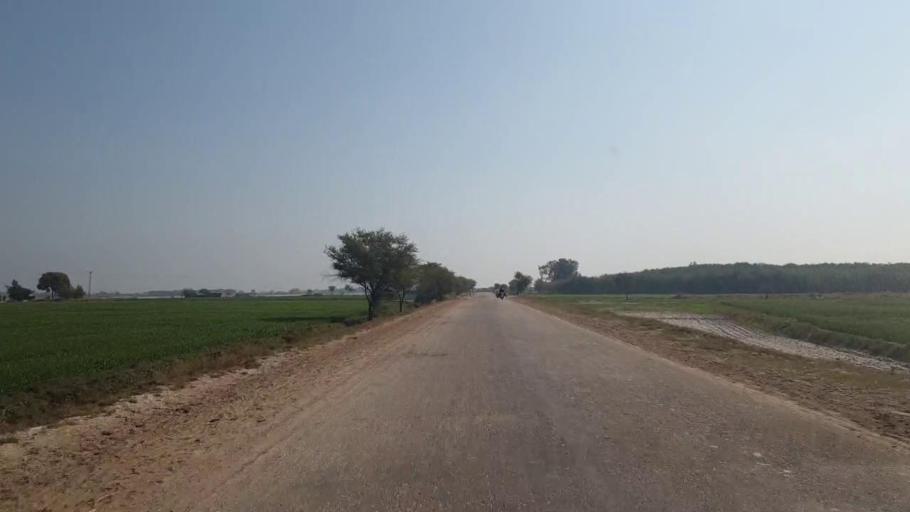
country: PK
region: Sindh
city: Sakrand
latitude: 26.0508
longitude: 68.4171
